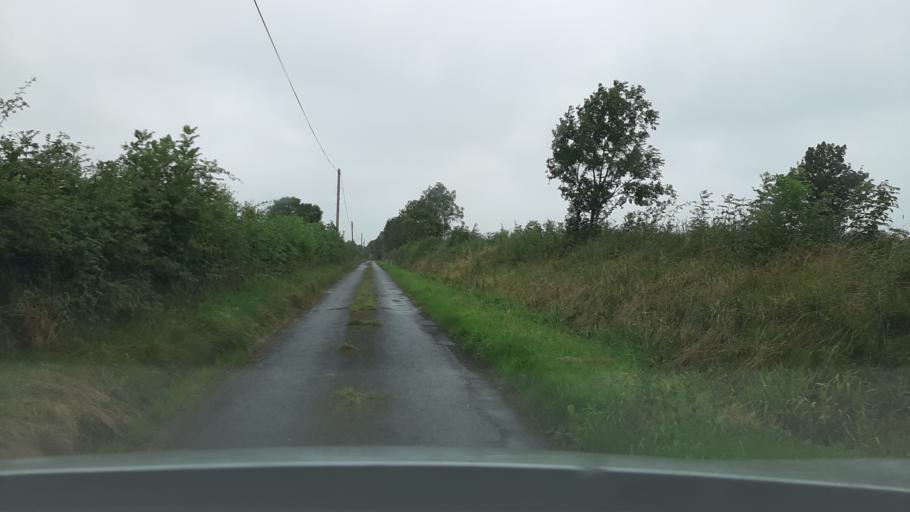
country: IE
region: Leinster
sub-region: Kildare
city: Rathangan
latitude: 53.1985
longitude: -7.0485
